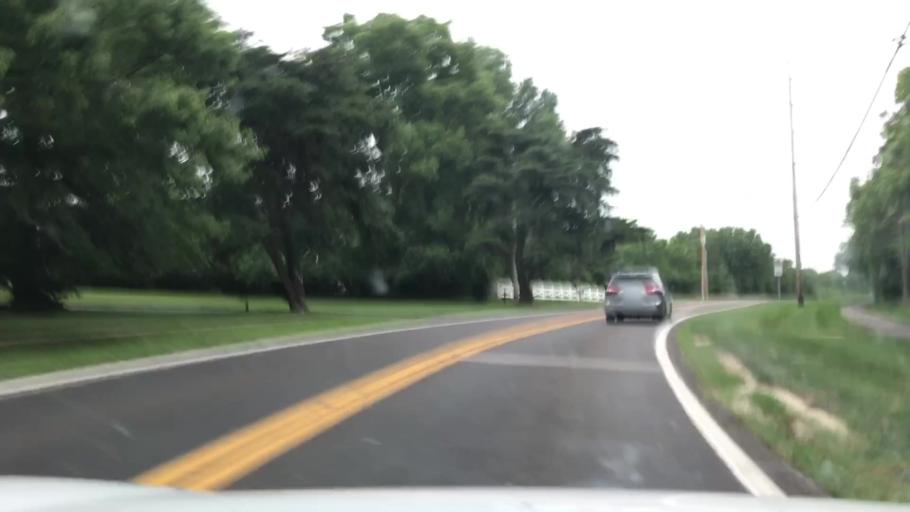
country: US
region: Missouri
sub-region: Saint Louis County
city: Clarkson Valley
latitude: 38.6266
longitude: -90.5918
